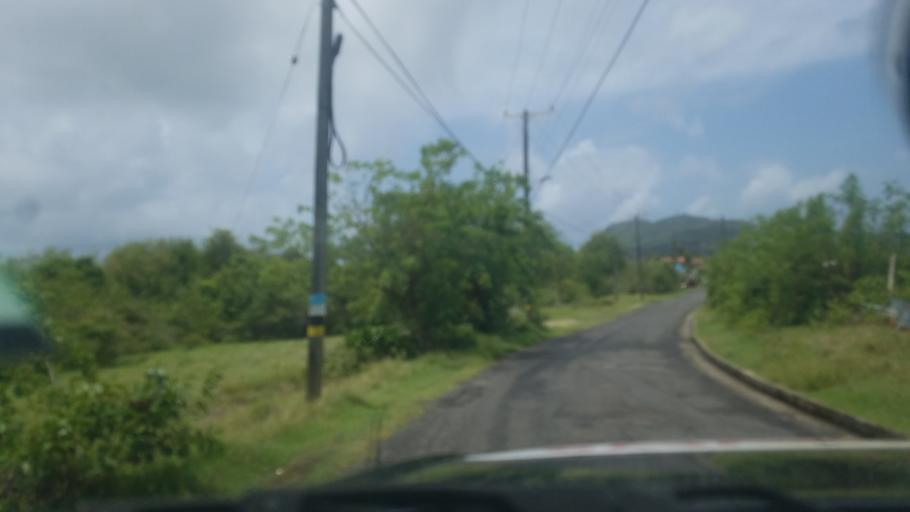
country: LC
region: Vieux-Fort
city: Vieux Fort
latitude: 13.7407
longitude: -60.9584
